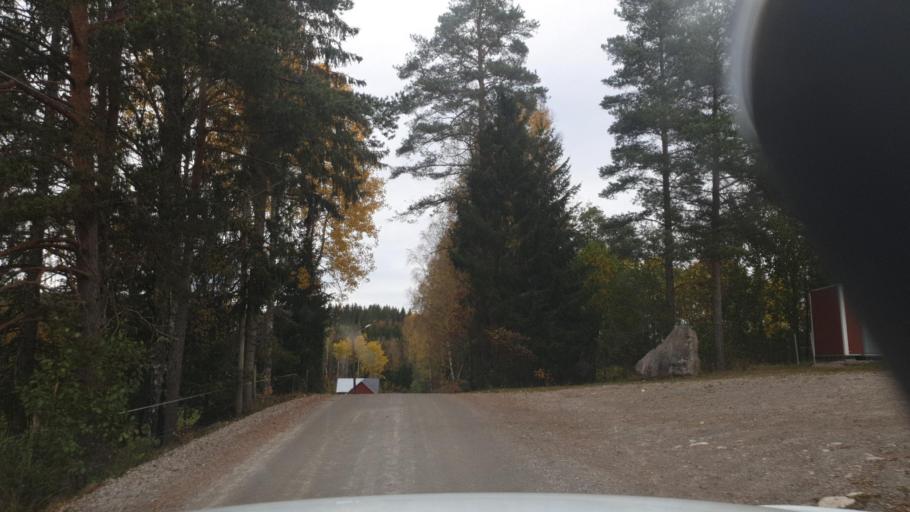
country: SE
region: Vaermland
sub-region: Arvika Kommun
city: Arvika
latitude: 59.6751
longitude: 12.7683
